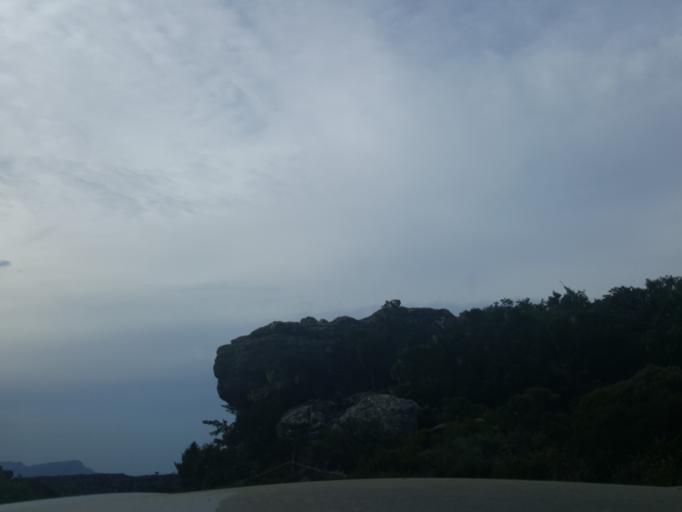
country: ZA
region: Limpopo
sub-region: Mopani District Municipality
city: Hoedspruit
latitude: -24.5518
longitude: 30.8695
